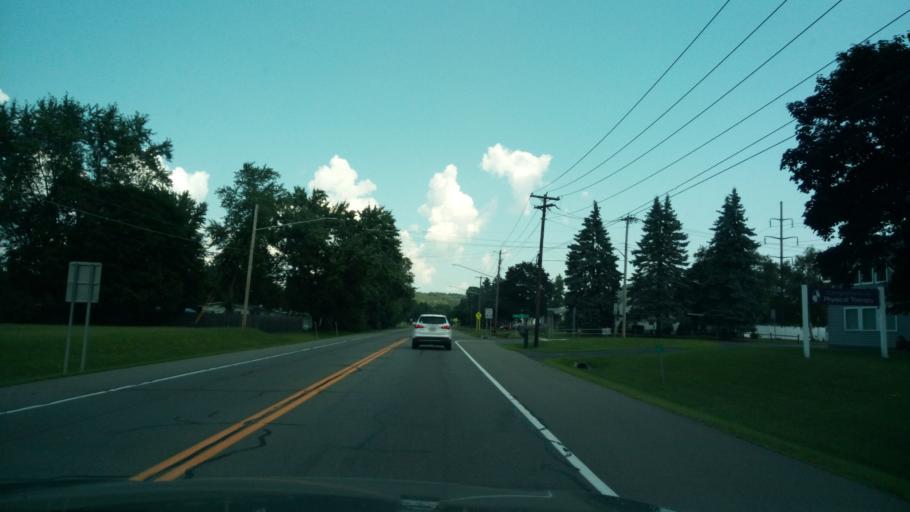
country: US
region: New York
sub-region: Chemung County
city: Horseheads
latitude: 42.1673
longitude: -76.8402
